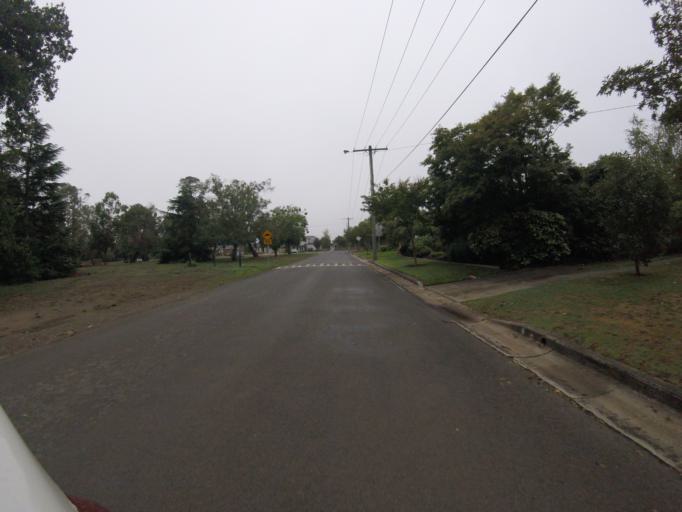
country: AU
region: Victoria
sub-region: Ballarat North
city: Newington
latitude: -37.5423
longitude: 143.8263
